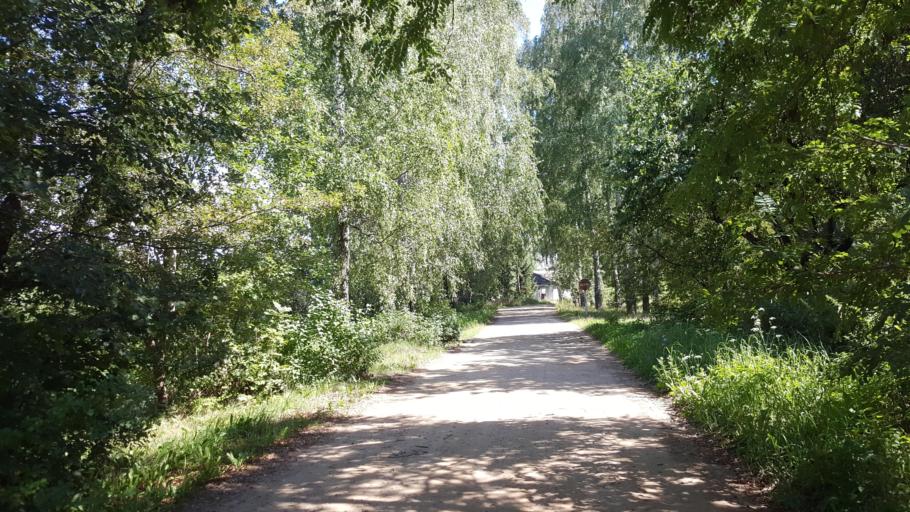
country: BY
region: Brest
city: Charnawchytsy
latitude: 52.2576
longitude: 23.5838
